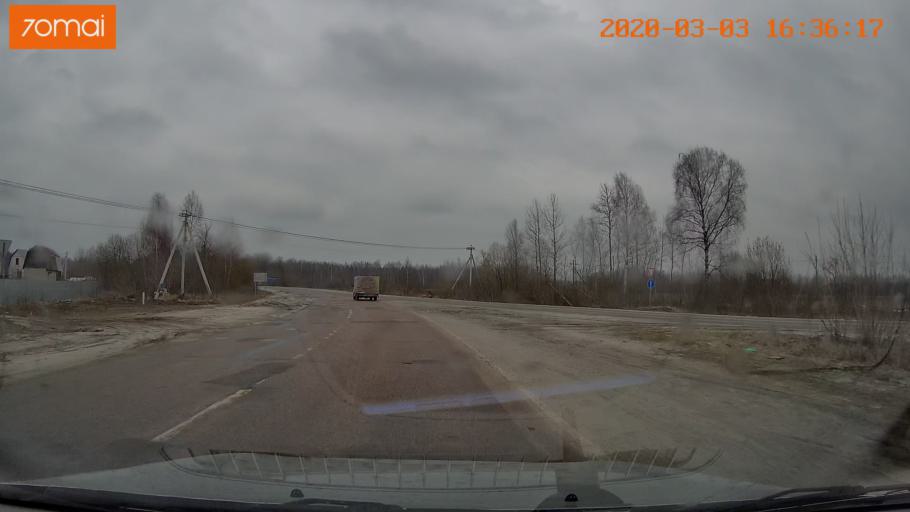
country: RU
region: Moskovskaya
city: Lopatinskiy
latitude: 55.3998
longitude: 38.7703
